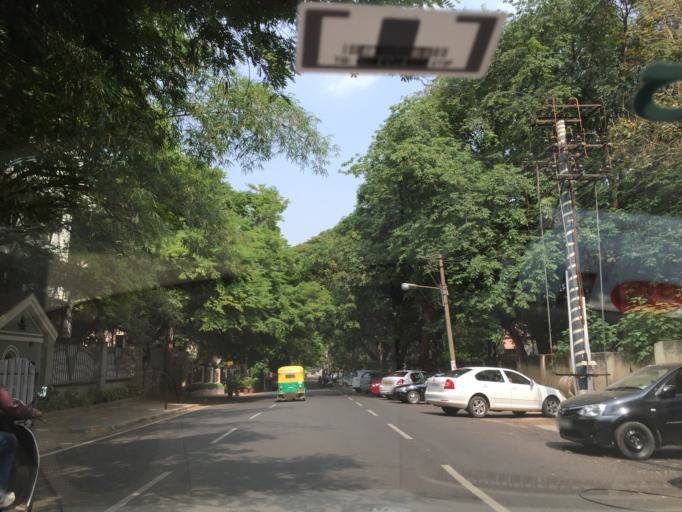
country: IN
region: Karnataka
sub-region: Bangalore Urban
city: Bangalore
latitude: 12.9860
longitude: 77.5926
